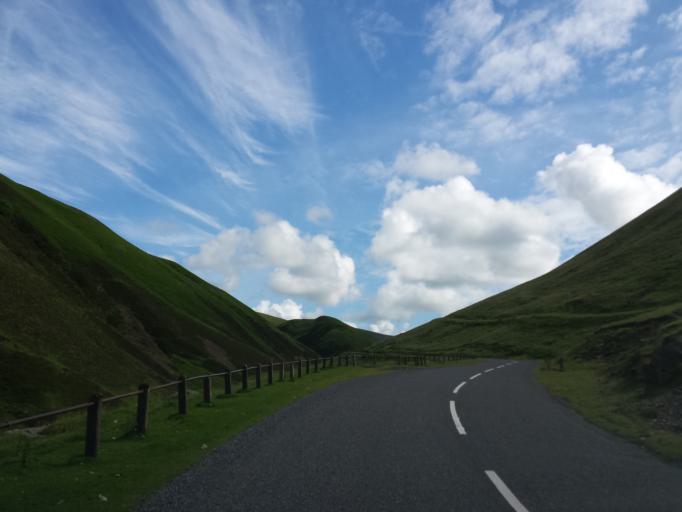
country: GB
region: Scotland
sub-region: Dumfries and Galloway
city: Moffat
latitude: 55.4218
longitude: -3.2784
